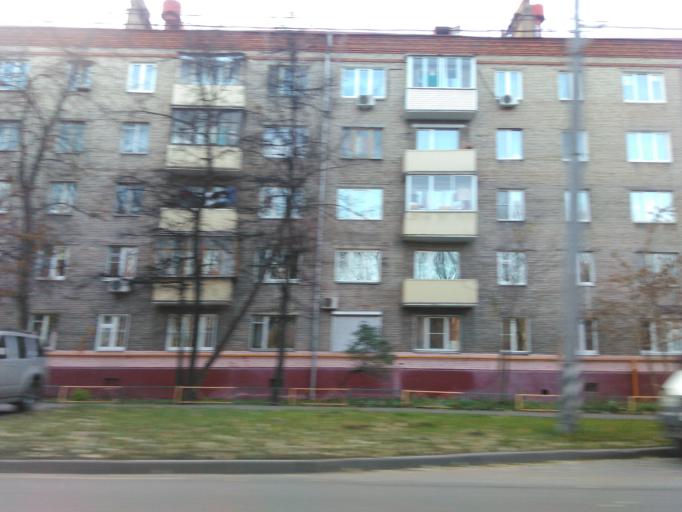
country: RU
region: Moscow
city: Ostankinskiy
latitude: 55.8275
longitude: 37.6016
